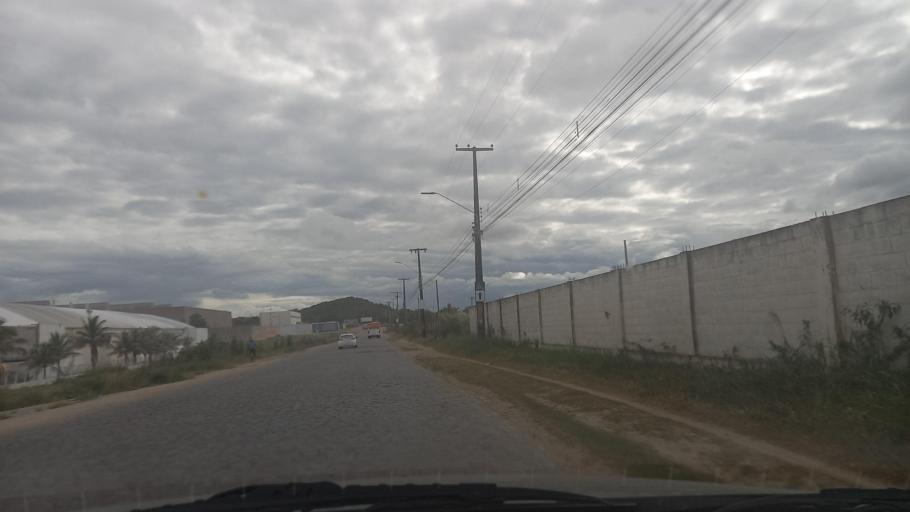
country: BR
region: Pernambuco
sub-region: Caruaru
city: Caruaru
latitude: -8.2892
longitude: -36.0145
